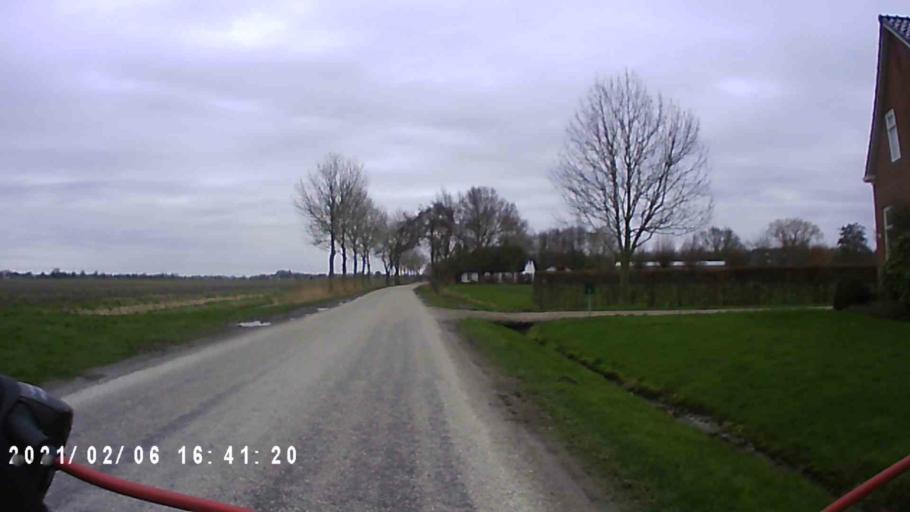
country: NL
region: Groningen
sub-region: Gemeente Bedum
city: Bedum
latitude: 53.4184
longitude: 6.7127
